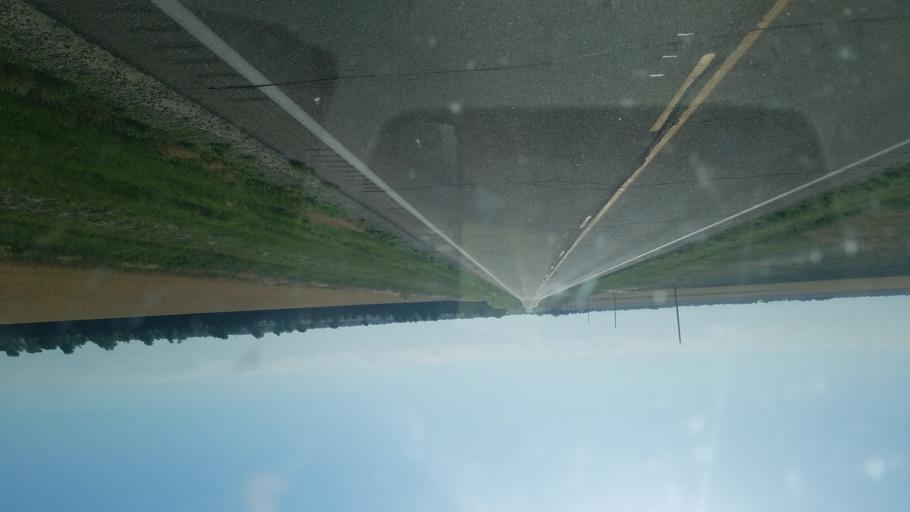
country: US
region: Kansas
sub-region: Pawnee County
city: Larned
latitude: 38.1888
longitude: -99.1385
